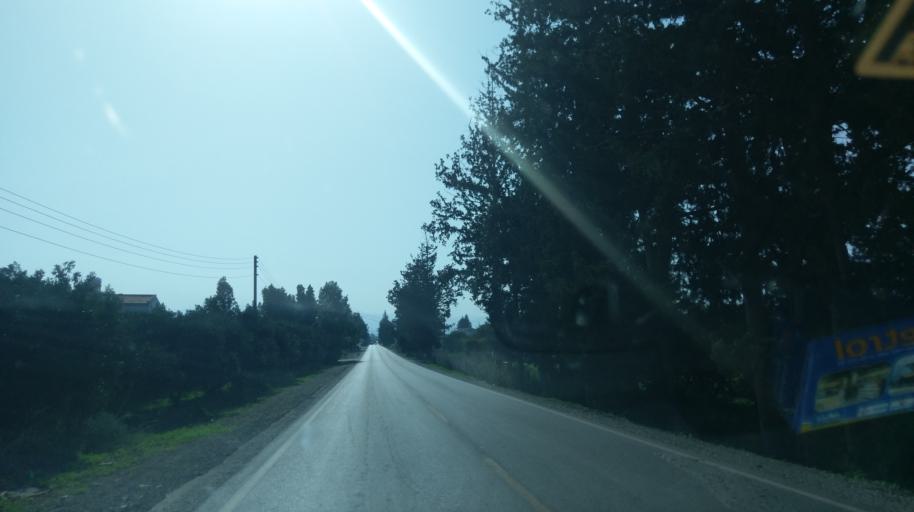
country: CY
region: Lefkosia
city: Morfou
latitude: 35.2242
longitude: 33.0104
